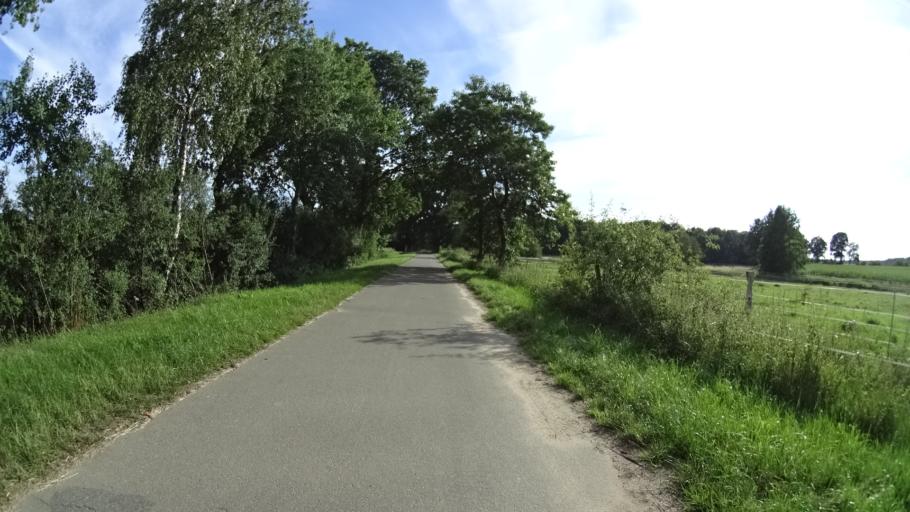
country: DE
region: Lower Saxony
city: Reppenstedt
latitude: 53.2415
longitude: 10.3594
